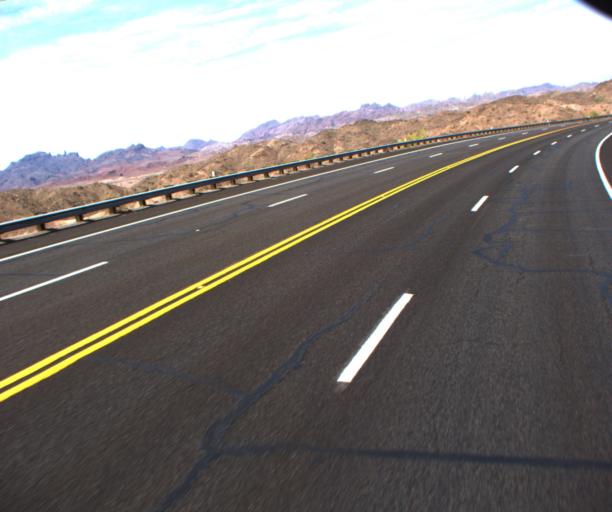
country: US
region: Arizona
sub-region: La Paz County
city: Cienega Springs
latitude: 34.1997
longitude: -114.2097
